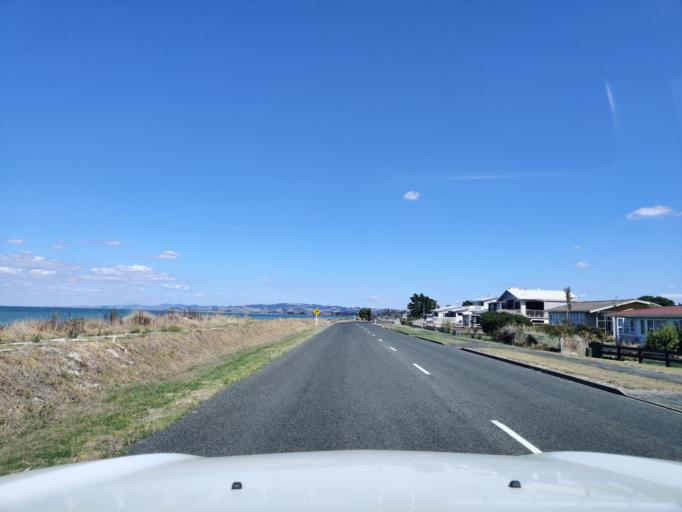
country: NZ
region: Waikato
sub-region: Thames-Coromandel District
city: Thames
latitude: -37.1075
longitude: 175.2991
